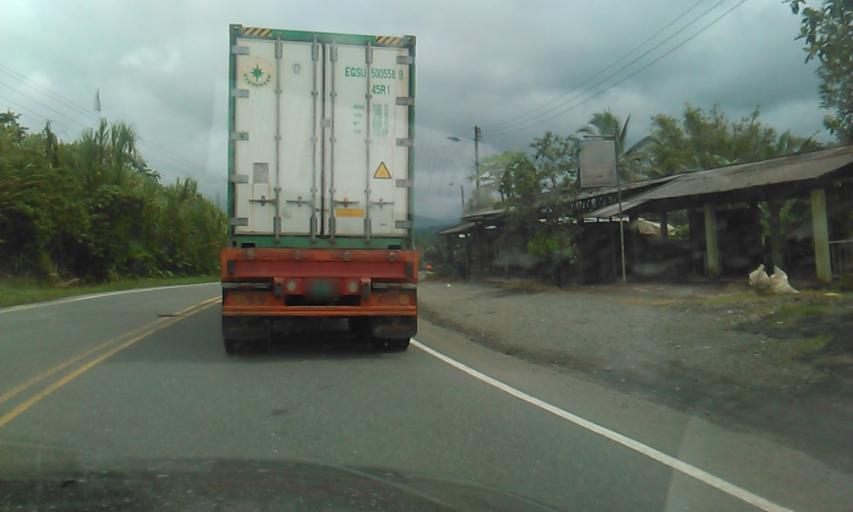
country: CO
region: Valle del Cauca
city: Buenaventura
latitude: 3.8830
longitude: -76.9527
